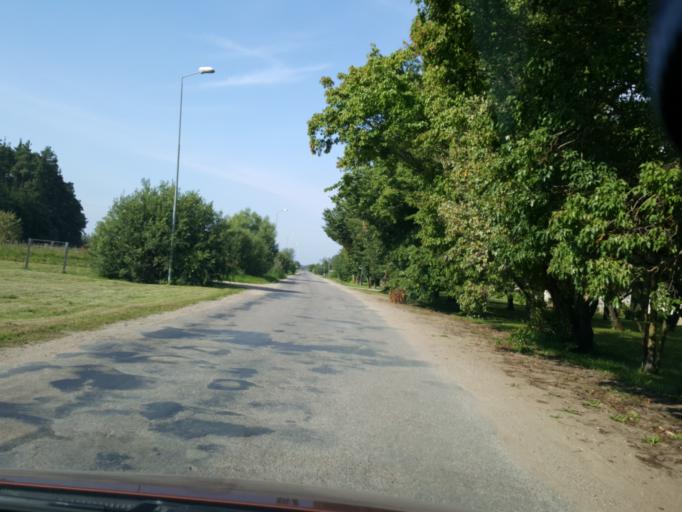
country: LV
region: Salacgrivas
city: Salacgriva
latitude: 57.7575
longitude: 24.4112
